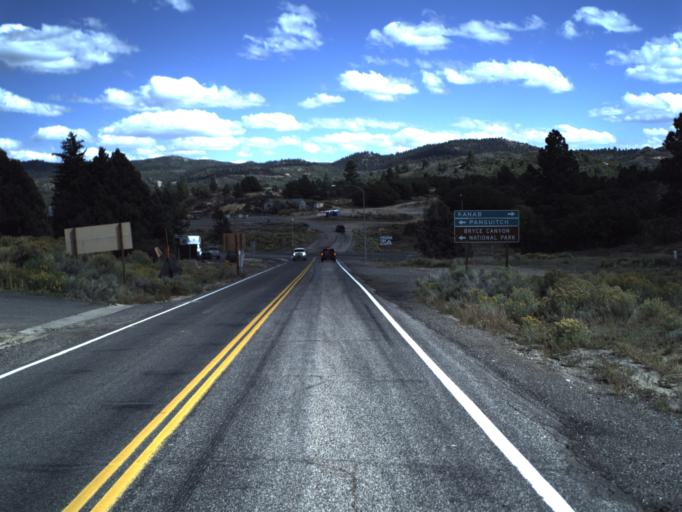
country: US
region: Utah
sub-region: Garfield County
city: Panguitch
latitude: 37.4890
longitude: -112.5147
